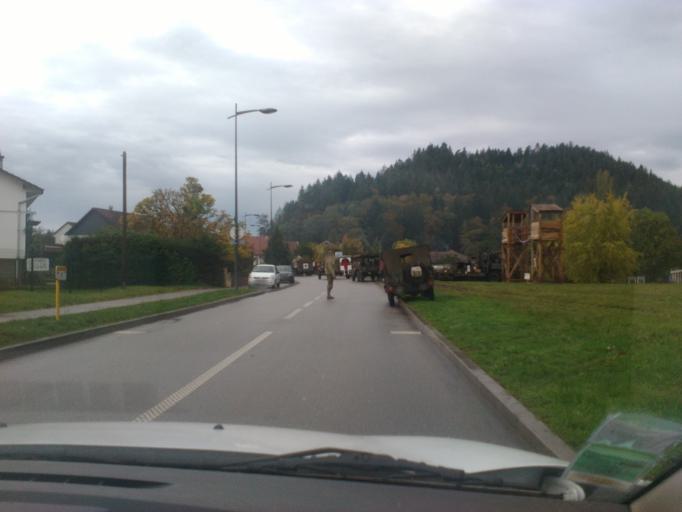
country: FR
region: Lorraine
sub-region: Departement des Vosges
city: Bruyeres
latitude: 48.2156
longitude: 6.7148
